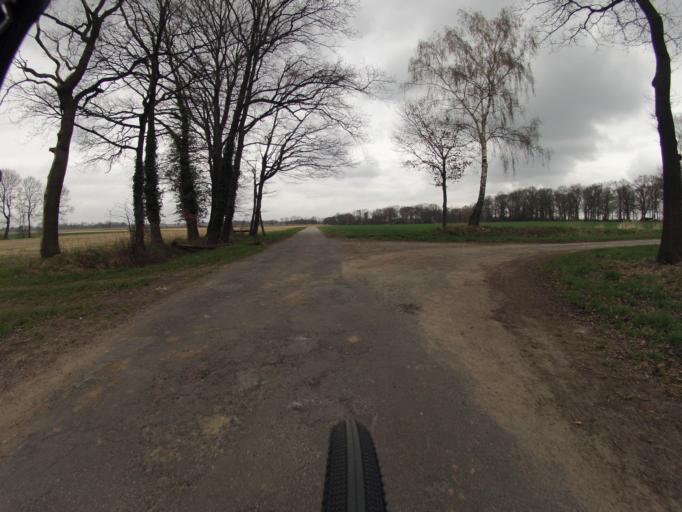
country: DE
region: North Rhine-Westphalia
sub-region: Regierungsbezirk Munster
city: Mettingen
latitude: 52.3341
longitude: 7.8184
